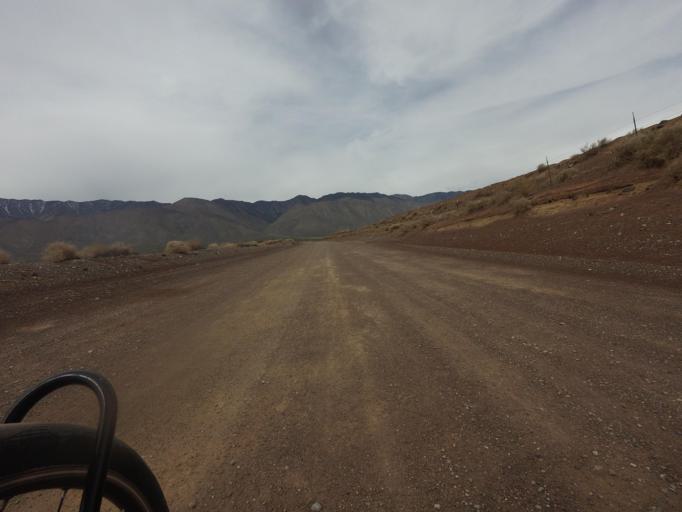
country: US
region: California
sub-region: Kern County
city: Inyokern
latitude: 35.9773
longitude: -117.9156
